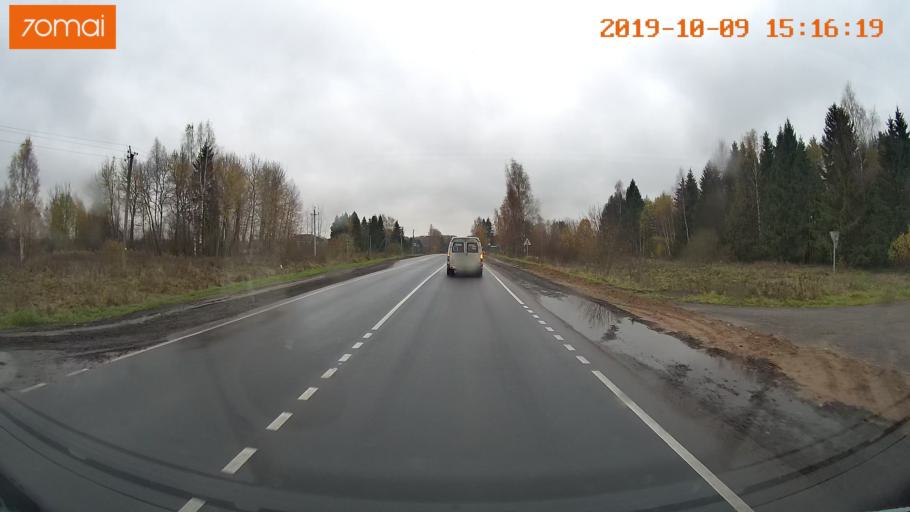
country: RU
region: Kostroma
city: Susanino
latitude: 58.1114
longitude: 41.5862
